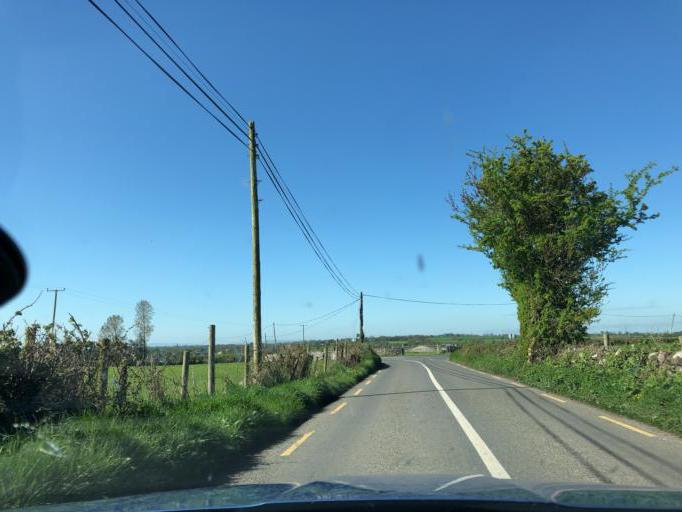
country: IE
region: Connaught
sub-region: County Galway
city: Portumna
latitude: 53.1909
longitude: -8.1615
